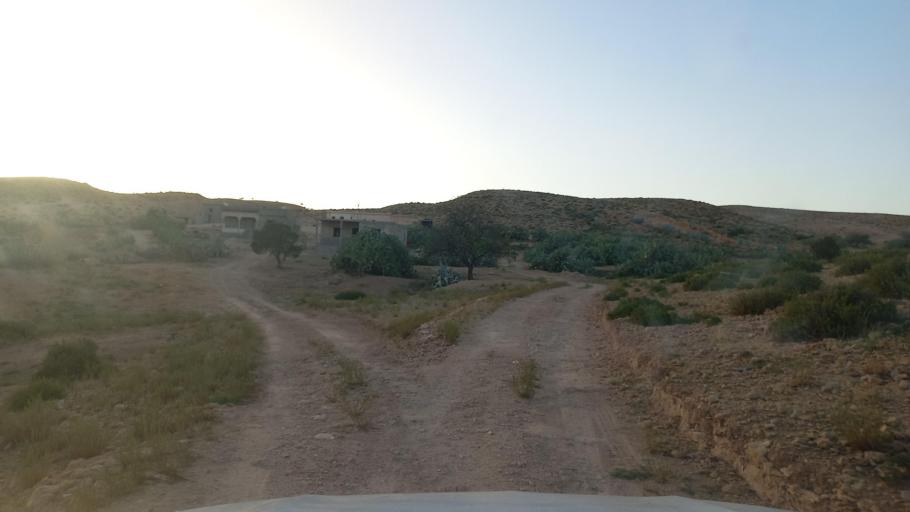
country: TN
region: Al Qasrayn
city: Sbiba
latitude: 35.3755
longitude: 9.0067
